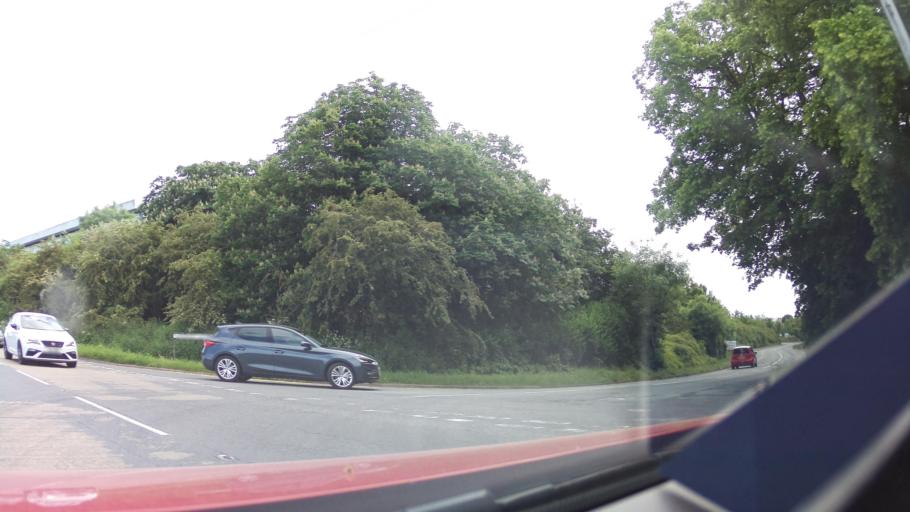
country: GB
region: England
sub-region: Worcestershire
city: Kempsey
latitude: 52.1605
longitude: -2.1598
